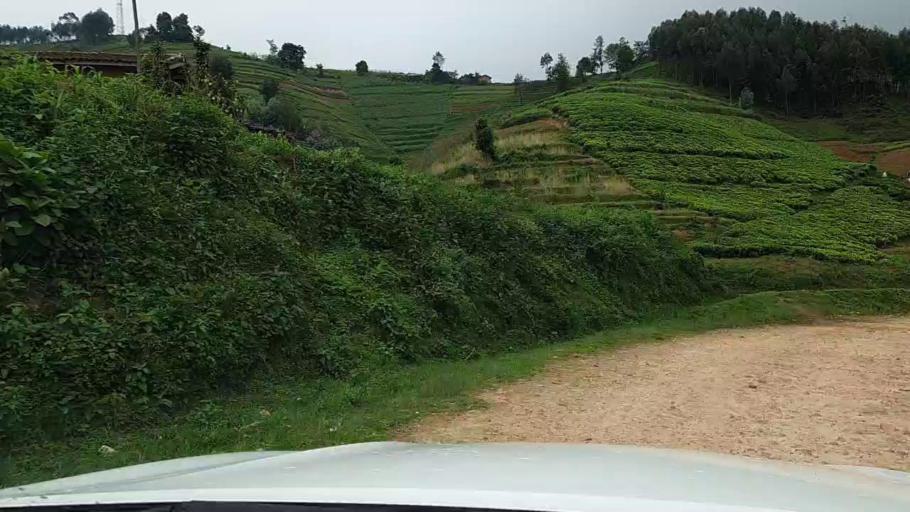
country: RW
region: Western Province
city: Kibuye
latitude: -2.2882
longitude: 29.3779
